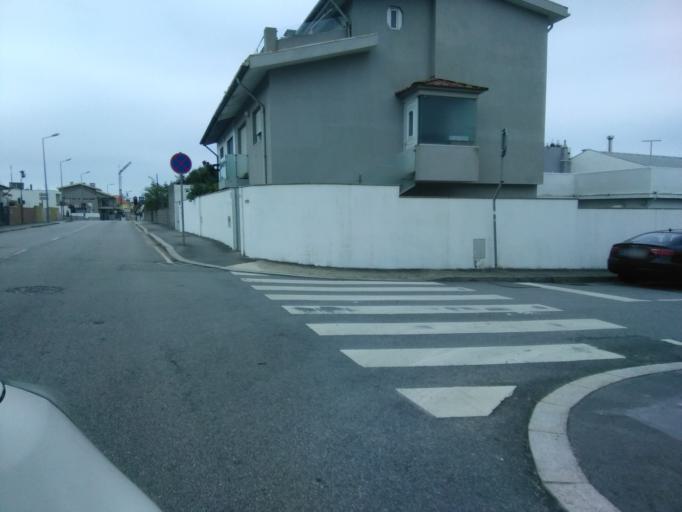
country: PT
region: Porto
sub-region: Matosinhos
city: Lavra
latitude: 41.2489
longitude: -8.7191
